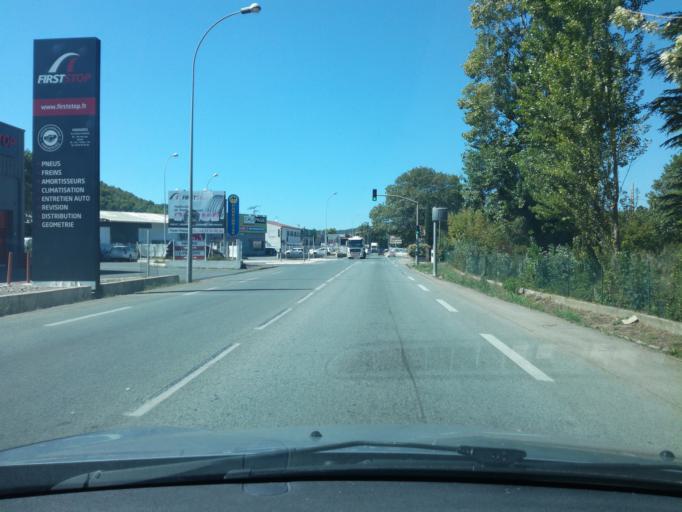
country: FR
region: Provence-Alpes-Cote d'Azur
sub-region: Departement du Var
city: Draguignan
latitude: 43.5219
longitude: 6.4664
